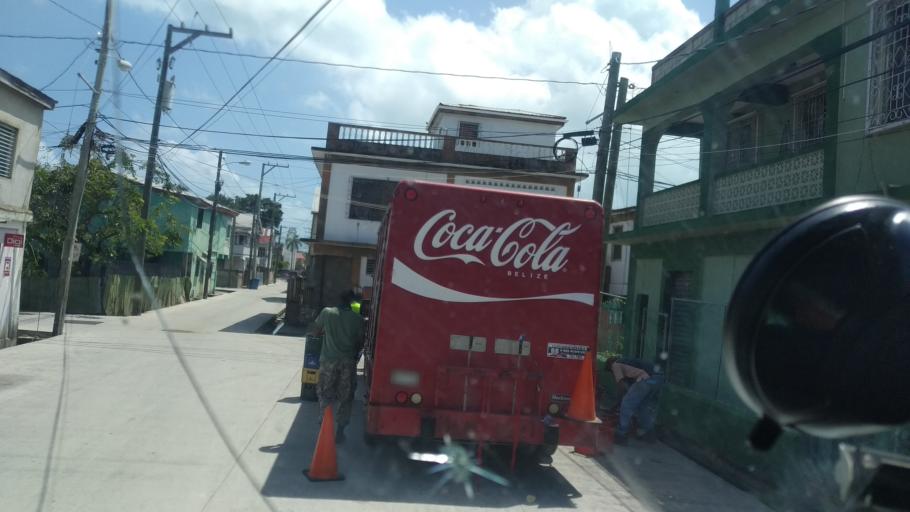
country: BZ
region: Belize
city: Belize City
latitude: 17.4914
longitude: -88.1907
